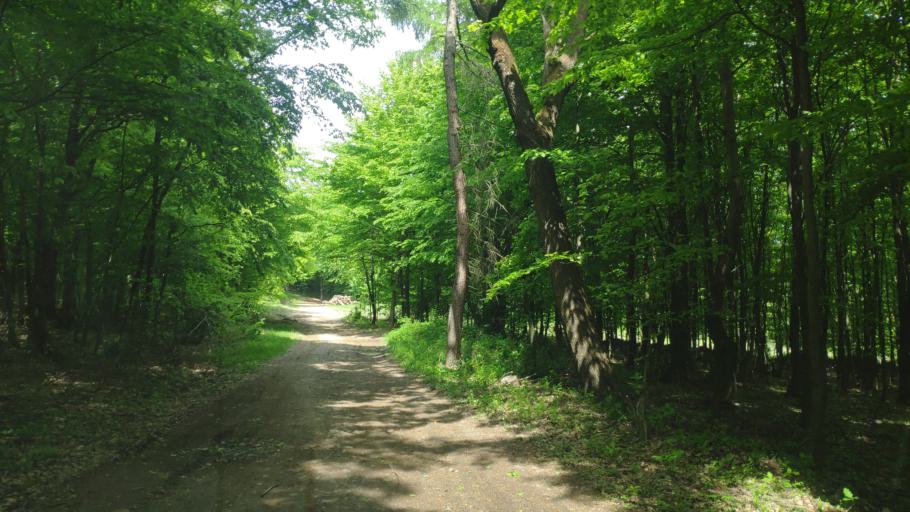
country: SK
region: Kosicky
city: Secovce
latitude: 48.7092
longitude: 21.5830
